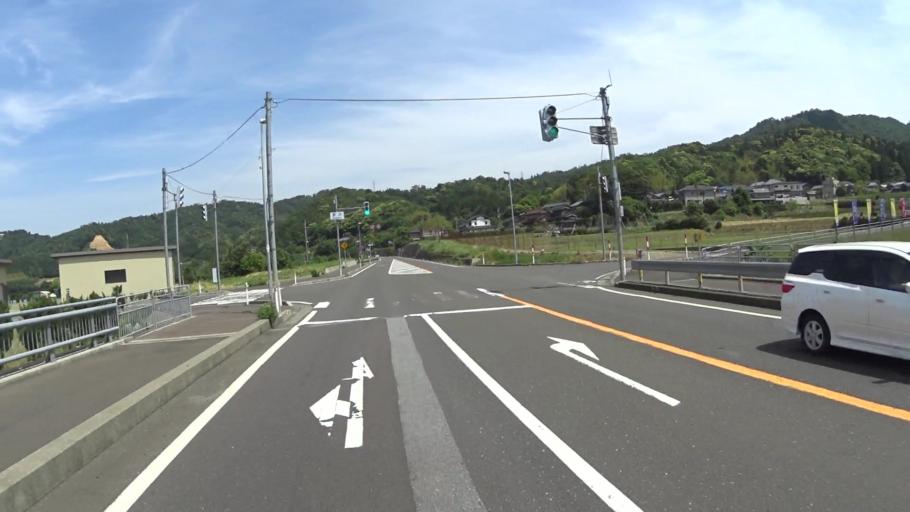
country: JP
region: Fukui
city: Obama
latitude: 35.4834
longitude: 135.7094
